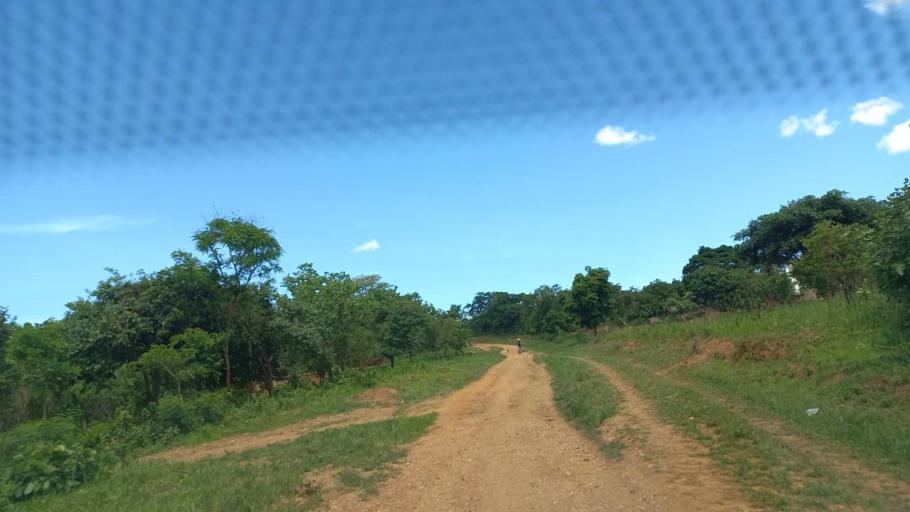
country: ZM
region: North-Western
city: Mwinilunga
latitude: -12.3600
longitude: 24.2309
